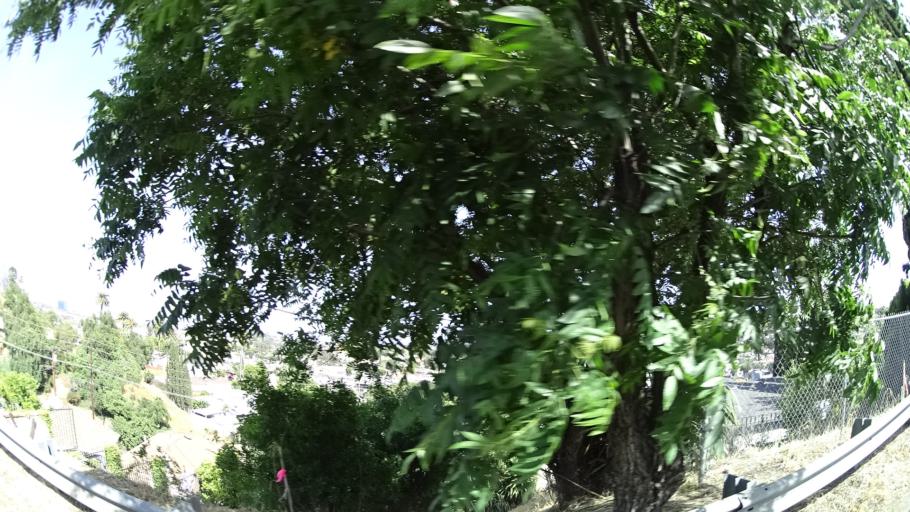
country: US
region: California
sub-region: Los Angeles County
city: Belvedere
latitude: 34.0745
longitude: -118.1743
